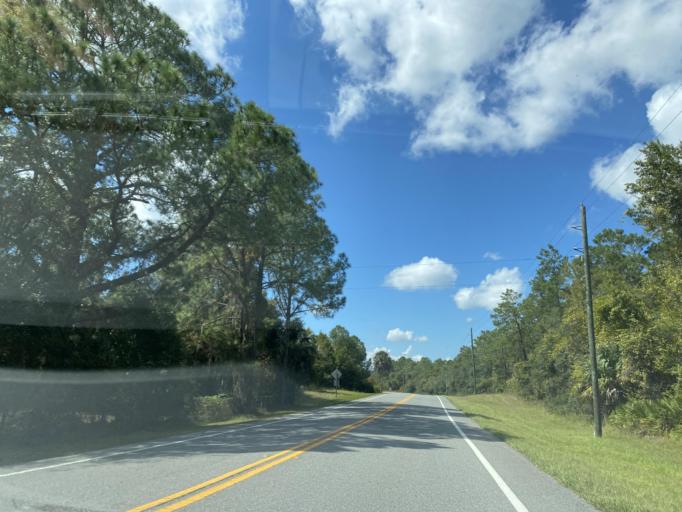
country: US
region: Florida
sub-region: Lake County
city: Lake Mack-Forest Hills
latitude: 29.0049
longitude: -81.4368
